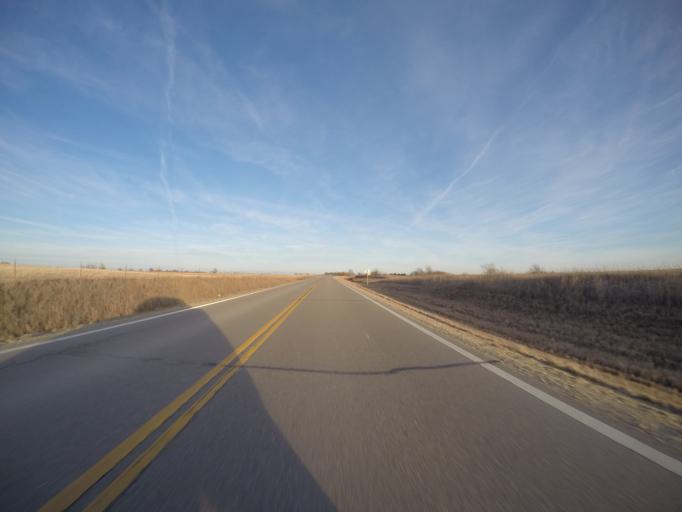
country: US
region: Kansas
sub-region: Dickinson County
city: Herington
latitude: 38.6603
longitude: -96.8508
